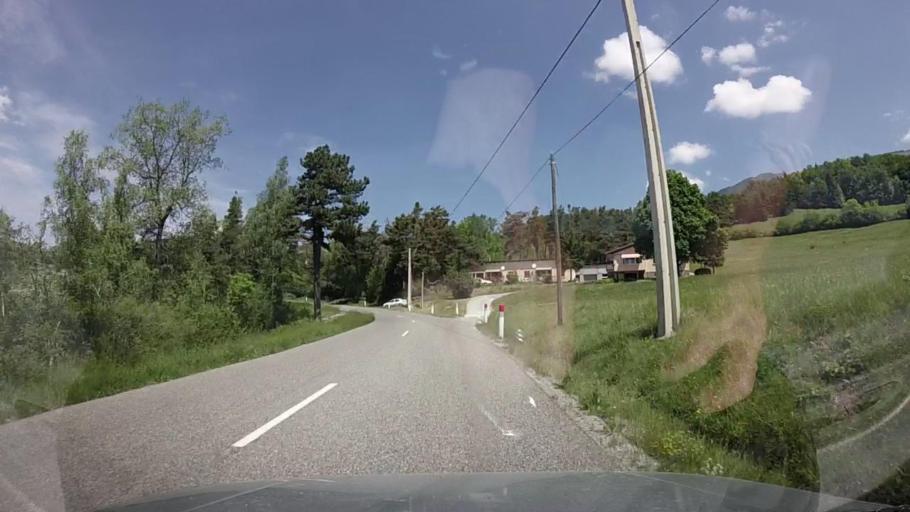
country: FR
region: Provence-Alpes-Cote d'Azur
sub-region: Departement des Alpes-de-Haute-Provence
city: Seyne-les-Alpes
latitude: 44.3797
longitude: 6.3519
